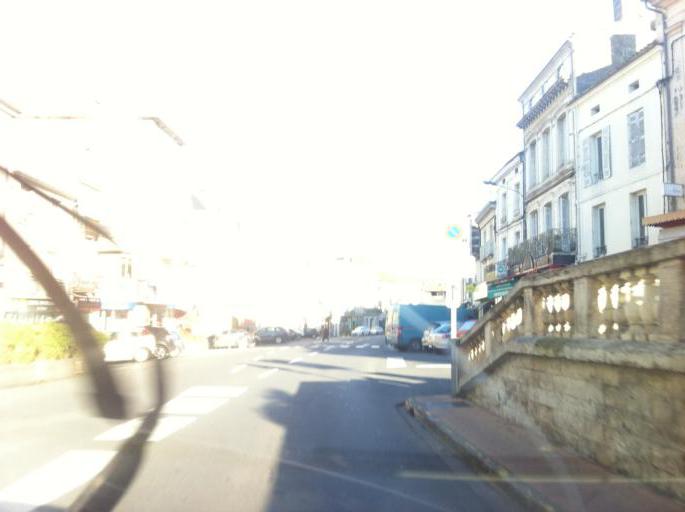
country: FR
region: Aquitaine
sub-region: Departement de la Dordogne
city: Riberac
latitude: 45.2468
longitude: 0.3401
